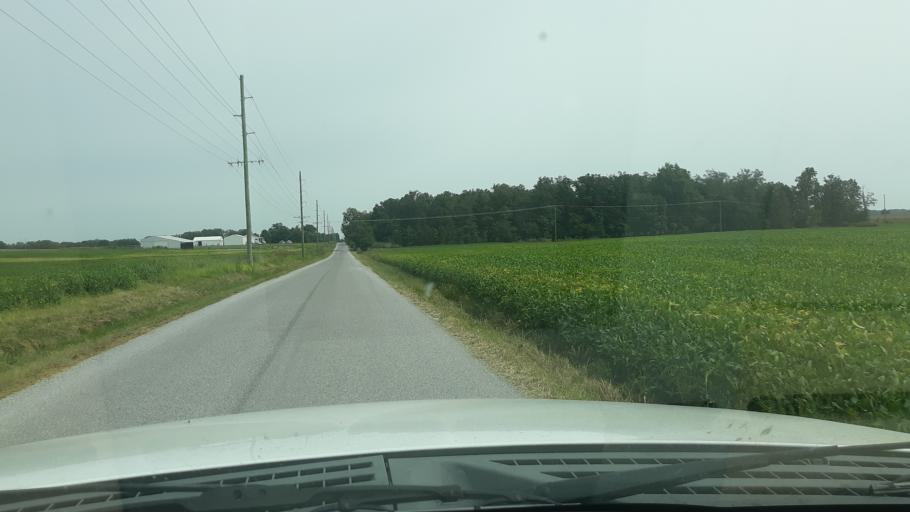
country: US
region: Illinois
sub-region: Saline County
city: Harrisburg
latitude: 37.8629
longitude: -88.5563
